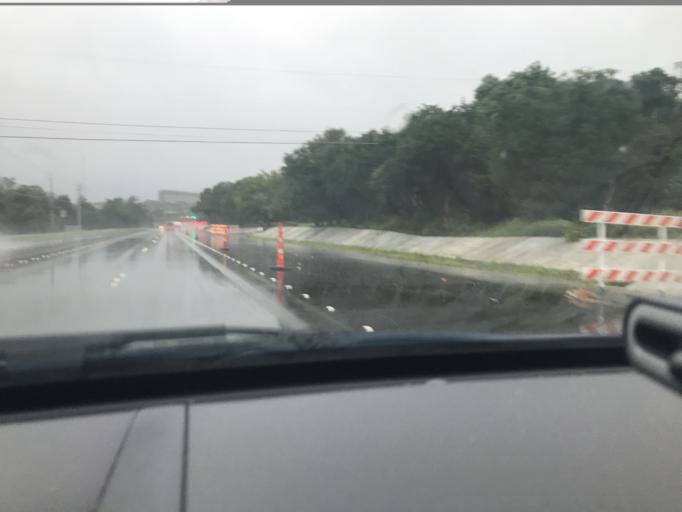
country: US
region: Texas
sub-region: Travis County
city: West Lake Hills
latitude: 30.2907
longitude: -97.8202
